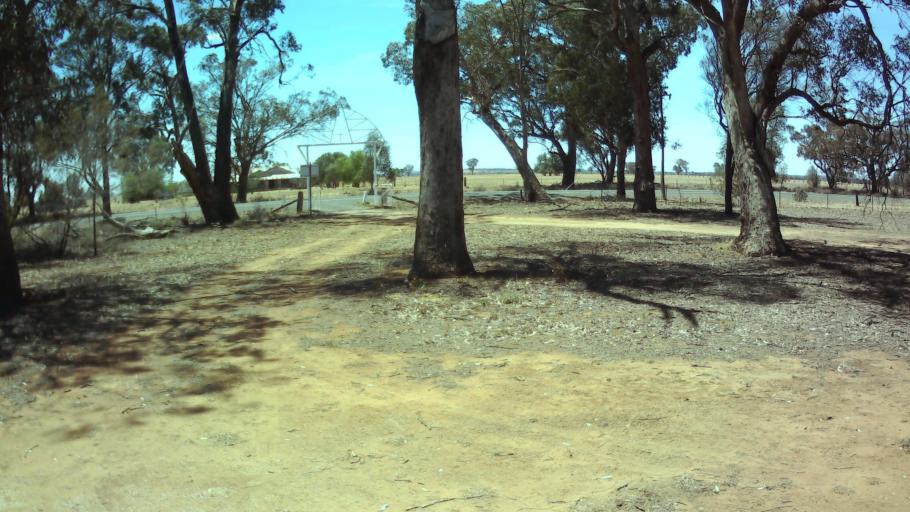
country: AU
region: New South Wales
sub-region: Weddin
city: Grenfell
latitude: -33.8427
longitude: 147.7241
